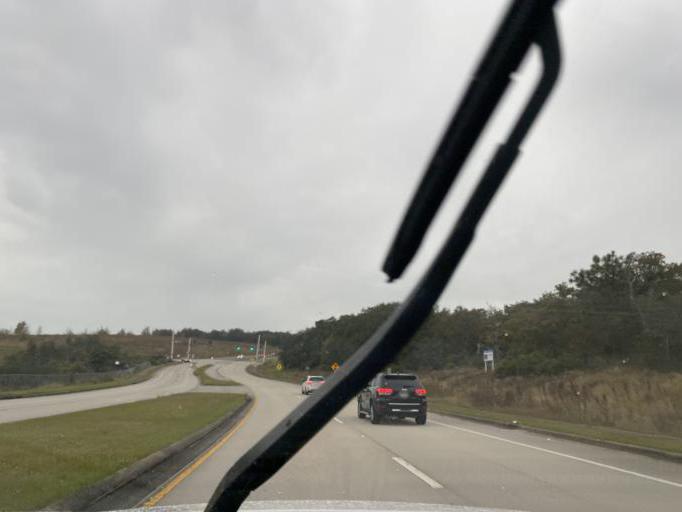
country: US
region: Florida
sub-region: Lake County
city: Minneola
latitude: 28.5442
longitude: -81.7156
